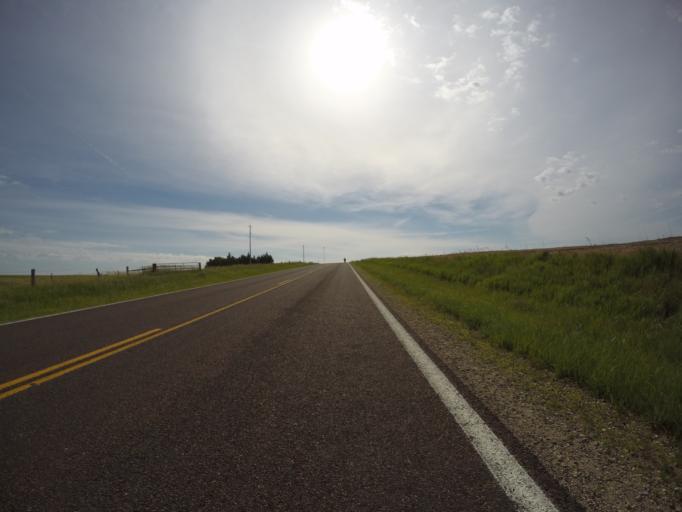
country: US
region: Kansas
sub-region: Washington County
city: Washington
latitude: 39.7118
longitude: -97.2479
